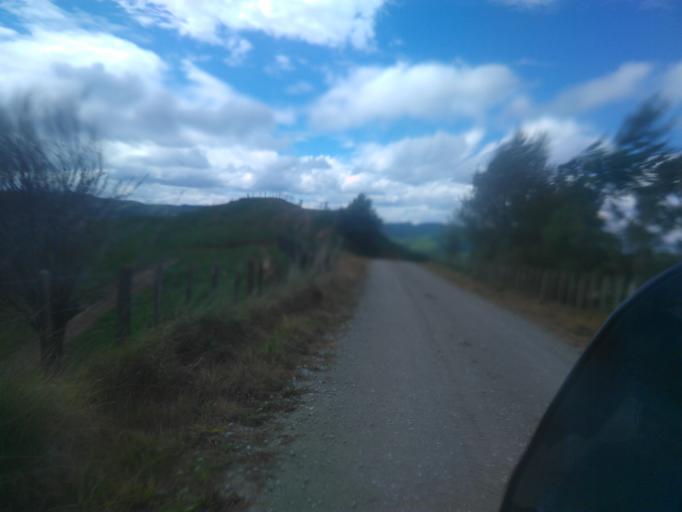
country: NZ
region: Gisborne
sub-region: Gisborne District
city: Gisborne
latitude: -38.7667
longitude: 177.6406
